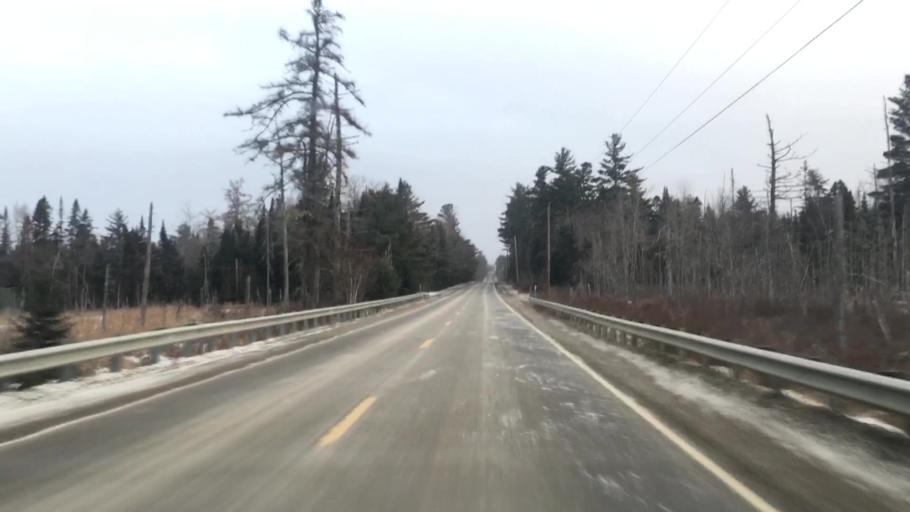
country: US
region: Maine
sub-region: Hancock County
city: Ellsworth
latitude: 44.6717
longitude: -68.3542
